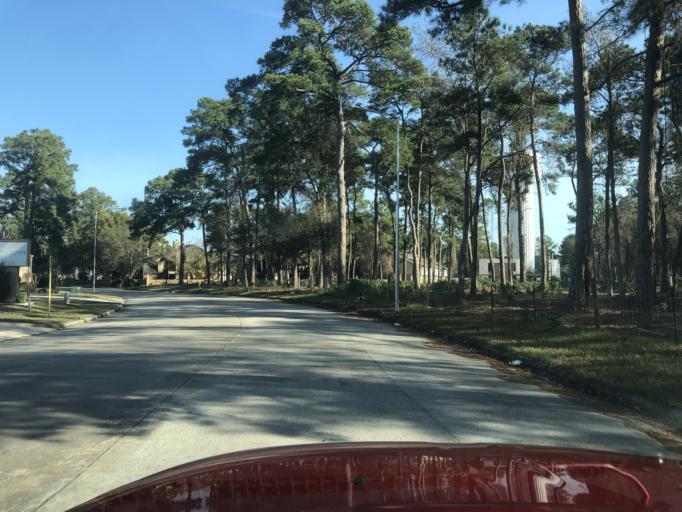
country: US
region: Texas
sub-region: Harris County
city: Spring
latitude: 30.0039
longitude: -95.4569
